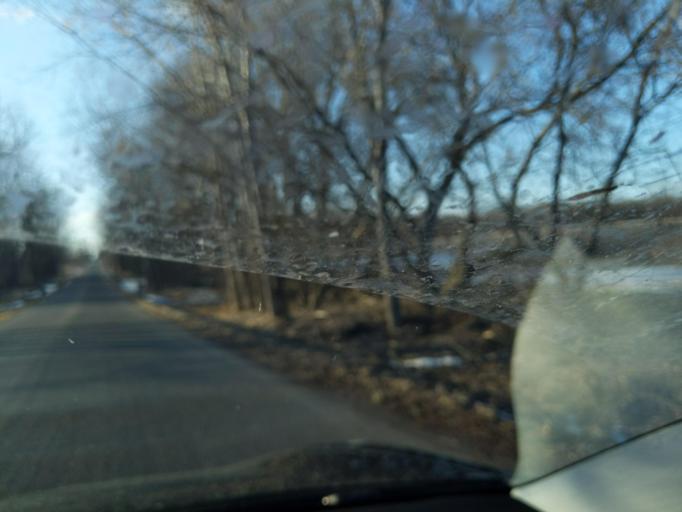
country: US
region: Michigan
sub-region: Ingham County
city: Stockbridge
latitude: 42.5200
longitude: -84.2456
